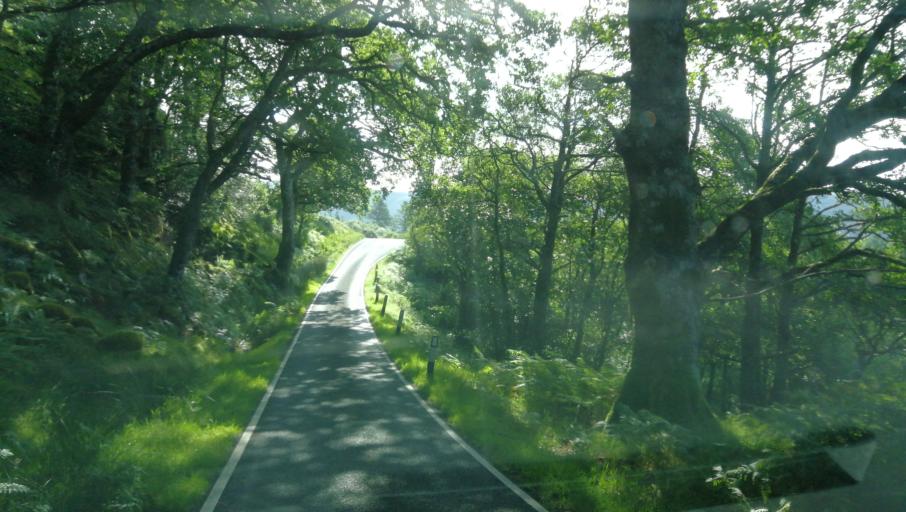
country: GB
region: Scotland
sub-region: Argyll and Bute
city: Isle Of Mull
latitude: 56.6787
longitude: -5.8400
